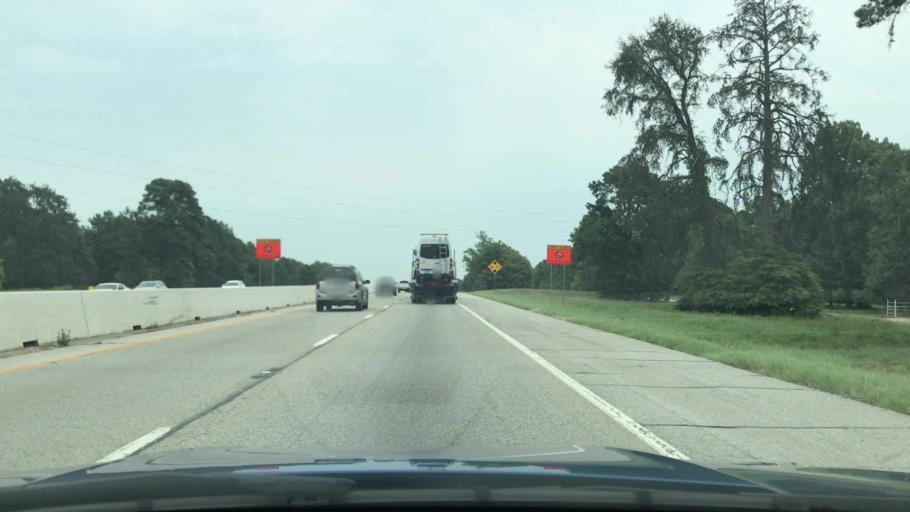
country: US
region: Texas
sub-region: Smith County
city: Hideaway
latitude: 32.4736
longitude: -95.4715
